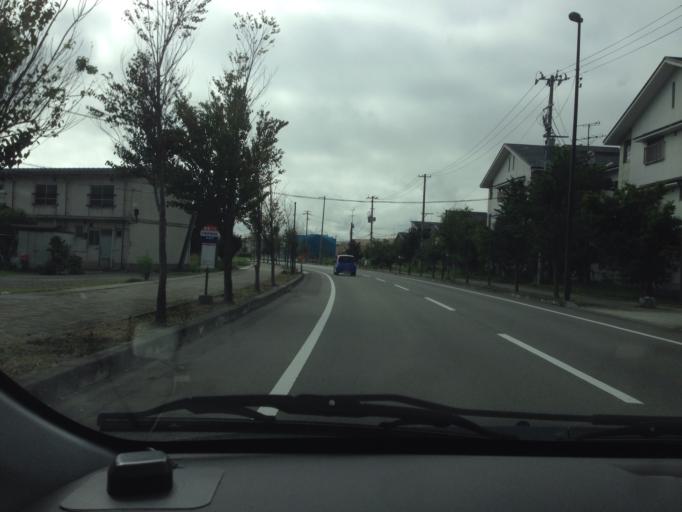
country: JP
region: Fukushima
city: Kitakata
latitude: 37.5615
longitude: 139.8105
